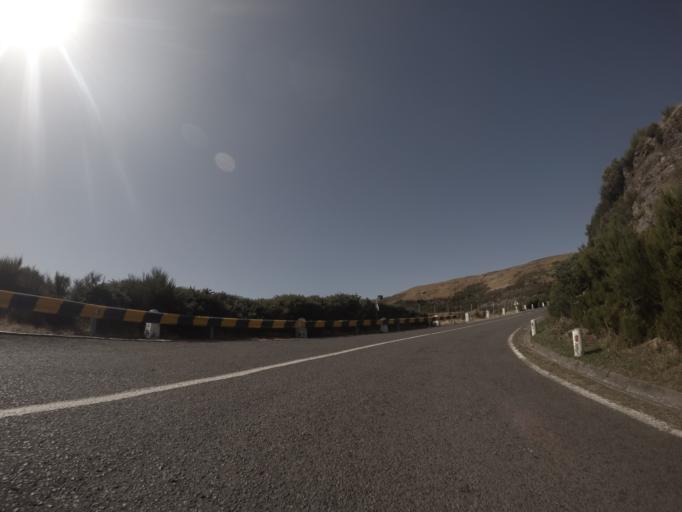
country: PT
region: Madeira
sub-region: Sao Vicente
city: Sao Vicente
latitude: 32.7323
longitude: -17.0575
